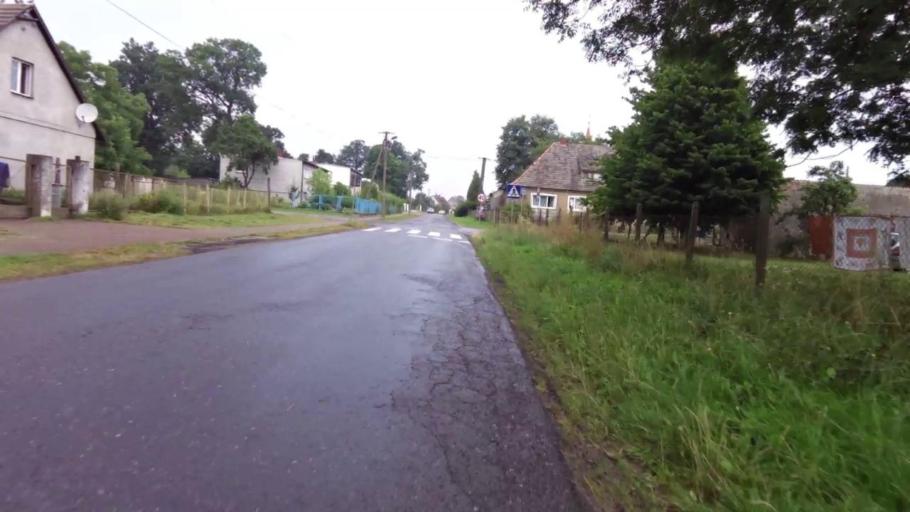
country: PL
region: West Pomeranian Voivodeship
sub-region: Powiat stargardzki
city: Insko
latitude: 53.4654
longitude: 15.5893
